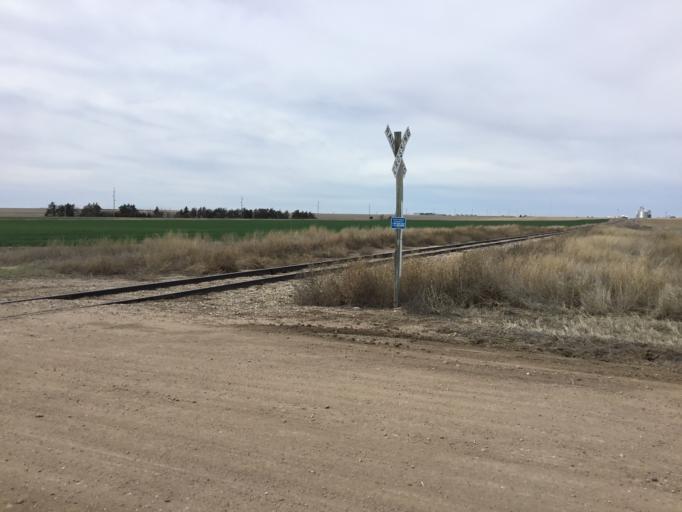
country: US
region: Kansas
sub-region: Sherman County
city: Goodland
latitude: 39.3387
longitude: -101.8559
